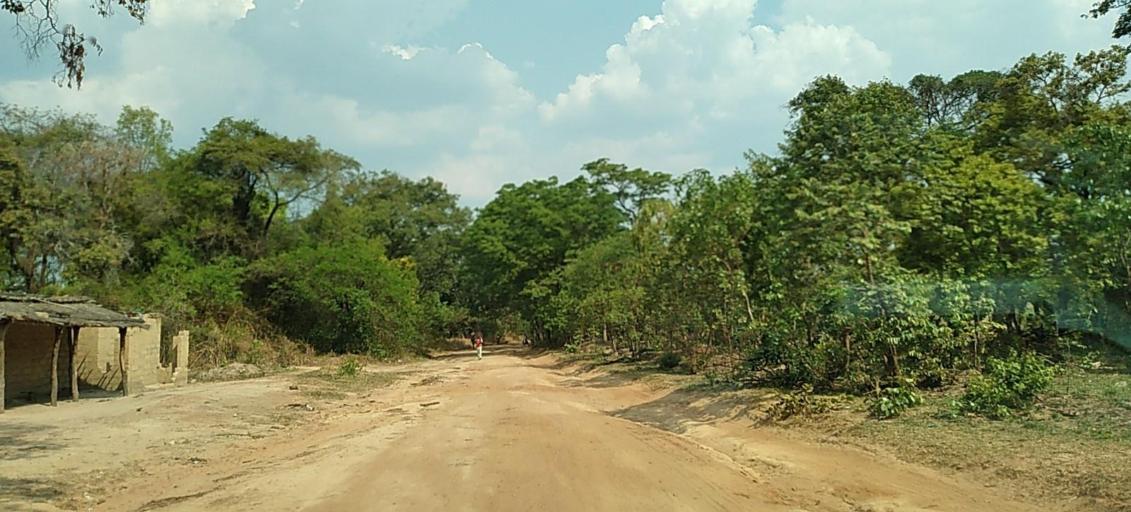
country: ZM
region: Copperbelt
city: Chingola
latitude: -12.7518
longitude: 27.7870
